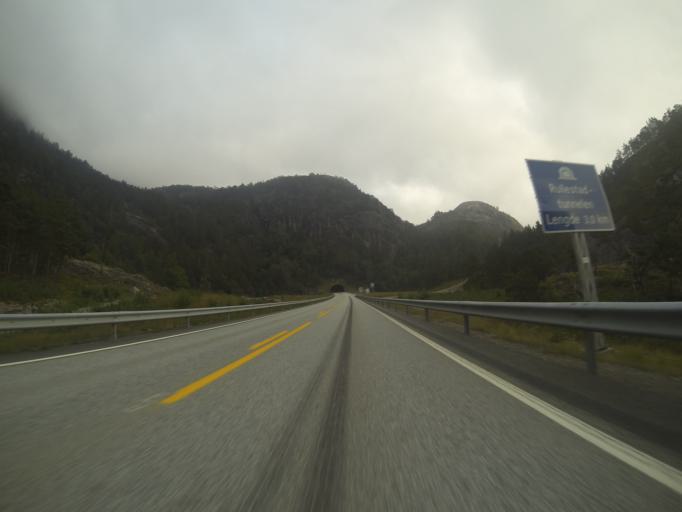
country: NO
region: Hordaland
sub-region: Odda
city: Odda
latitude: 59.8802
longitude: 6.4387
